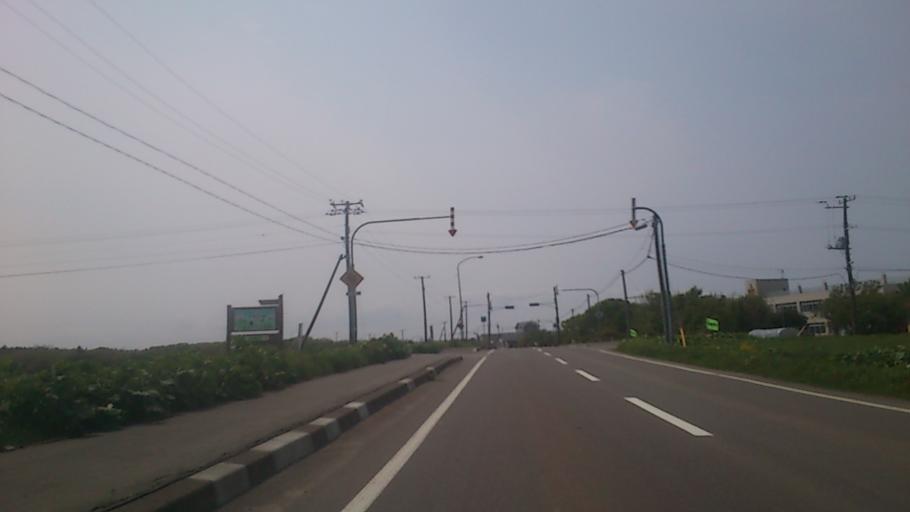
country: JP
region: Hokkaido
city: Nemuro
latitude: 43.2780
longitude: 145.5212
